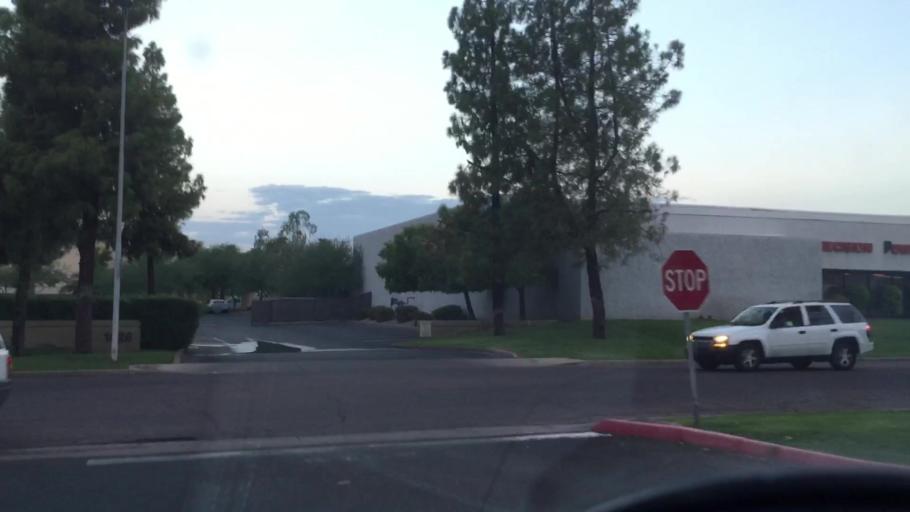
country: US
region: Arizona
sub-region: Maricopa County
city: Tempe Junction
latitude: 33.4105
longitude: -111.9674
